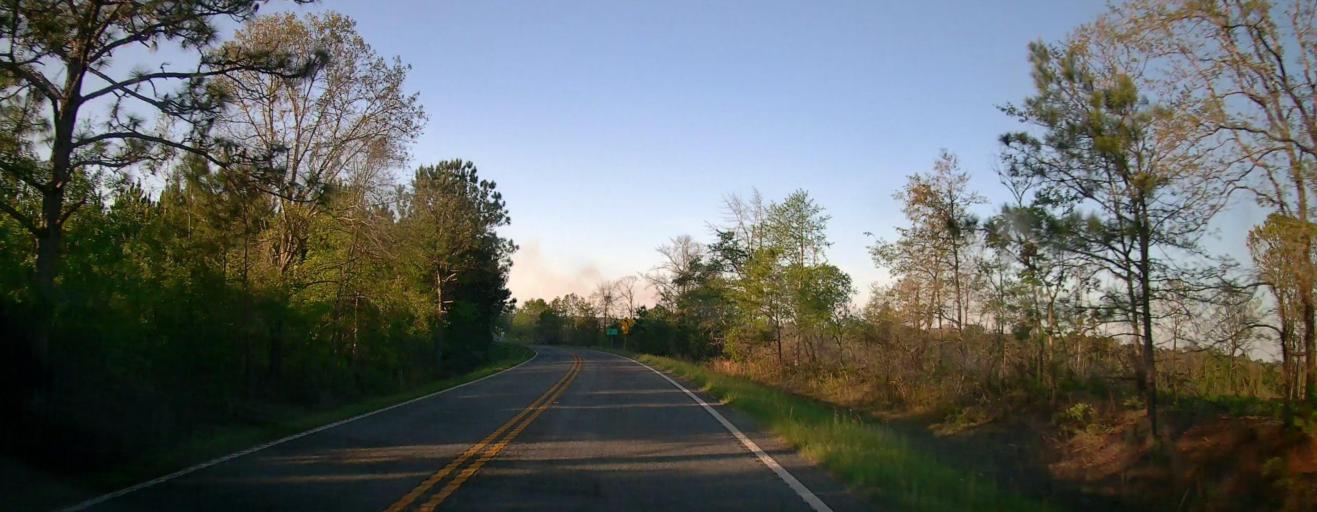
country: US
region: Georgia
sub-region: Marion County
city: Buena Vista
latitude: 32.4297
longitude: -84.4287
